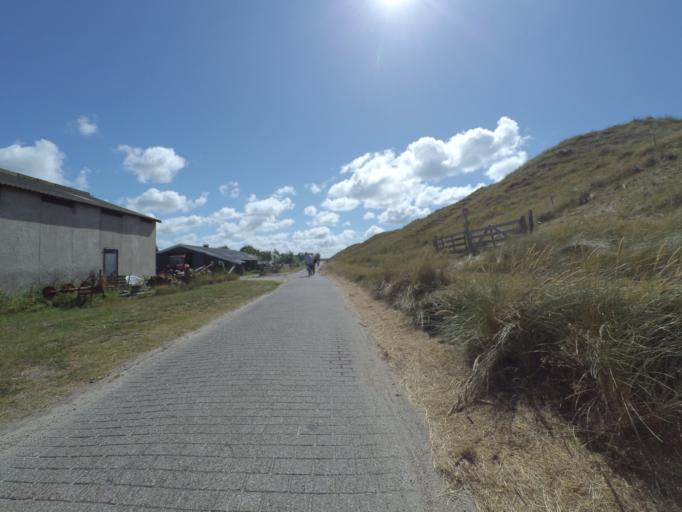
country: NL
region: North Holland
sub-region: Gemeente Texel
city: Den Burg
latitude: 53.1163
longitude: 4.7995
